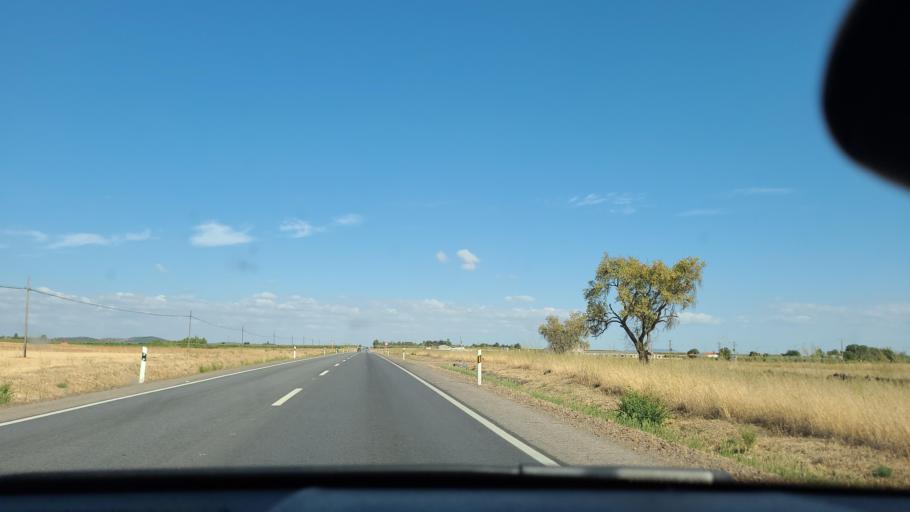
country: ES
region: Extremadura
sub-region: Provincia de Badajoz
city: Puebla de Sancho Perez
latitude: 38.4083
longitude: -6.3789
